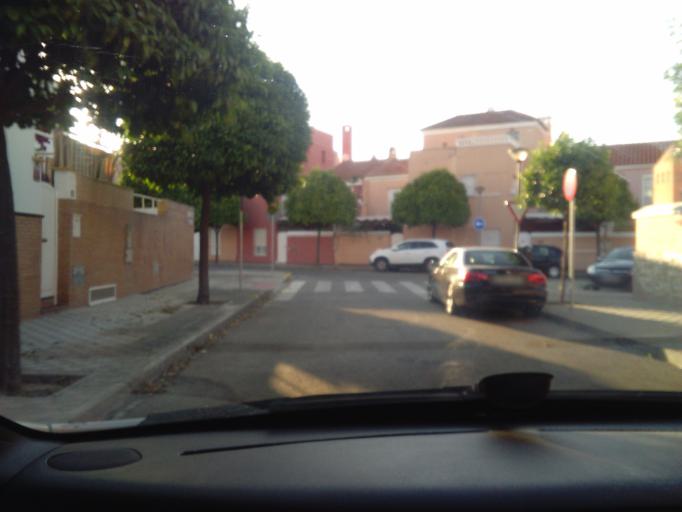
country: ES
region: Andalusia
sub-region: Provincia de Sevilla
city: Sevilla
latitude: 37.4044
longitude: -5.9435
